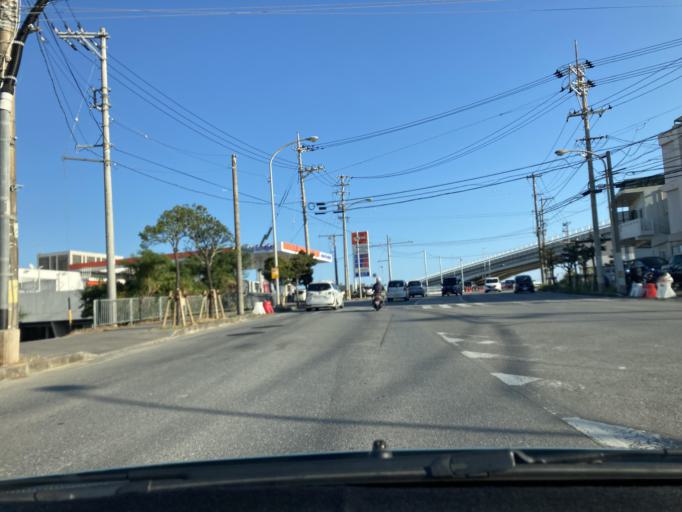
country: JP
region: Okinawa
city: Ginowan
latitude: 26.2432
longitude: 127.7394
